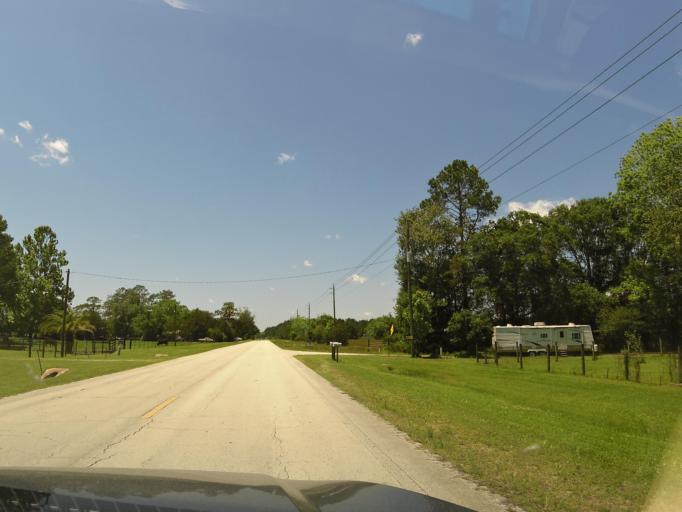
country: US
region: Florida
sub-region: Bradford County
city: Starke
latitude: 30.0461
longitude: -82.1310
